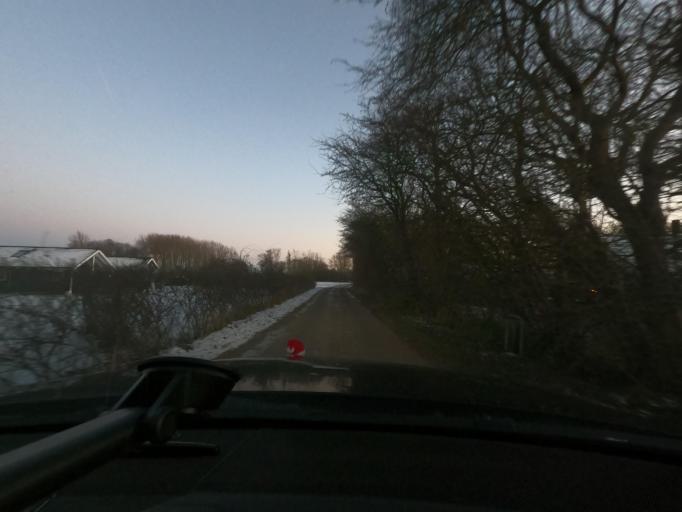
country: DK
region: South Denmark
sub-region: Sonderborg Kommune
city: Horuphav
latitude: 54.8714
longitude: 9.8886
